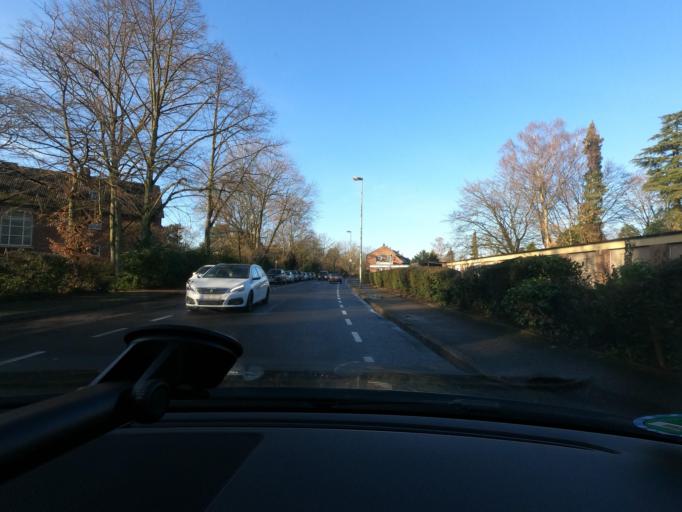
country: DE
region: North Rhine-Westphalia
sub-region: Regierungsbezirk Dusseldorf
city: Krefeld
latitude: 51.3491
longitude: 6.6069
